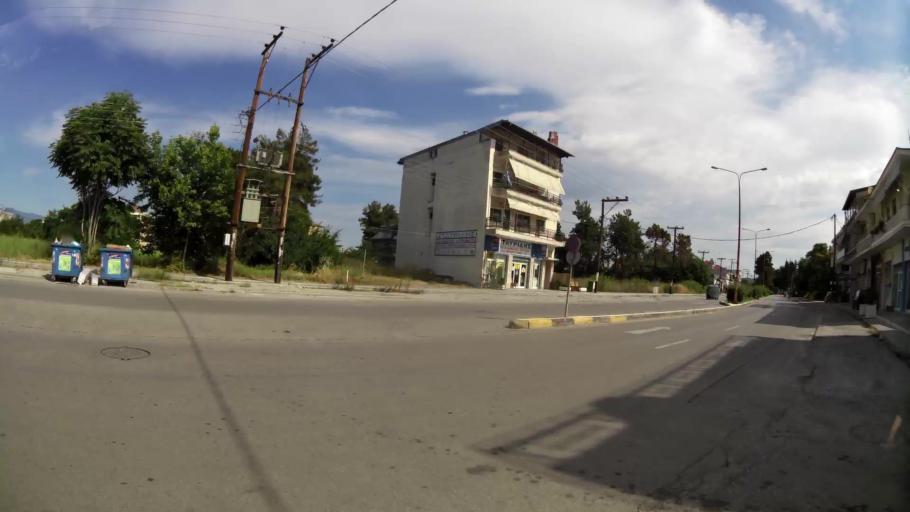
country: GR
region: Central Macedonia
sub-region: Nomos Pierias
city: Katerini
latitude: 40.2786
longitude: 22.5162
